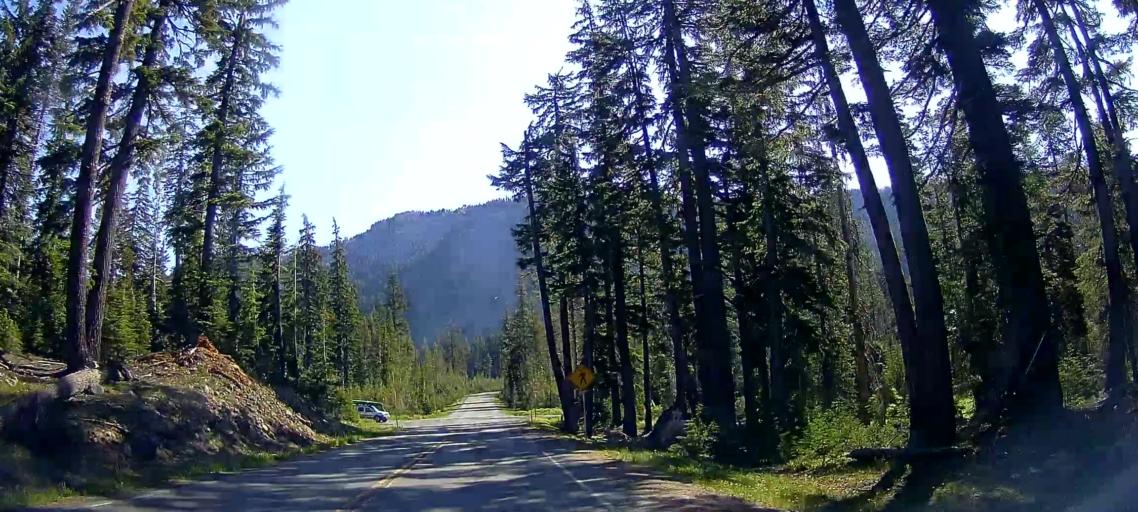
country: US
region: Oregon
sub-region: Jackson County
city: Shady Cove
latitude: 42.8940
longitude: -122.1378
